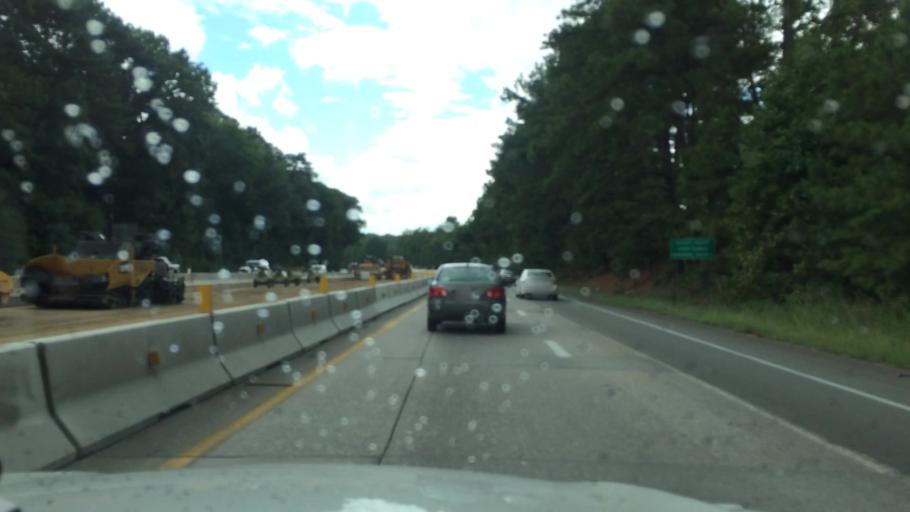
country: US
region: South Carolina
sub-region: Lexington County
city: Oak Grove
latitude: 34.0039
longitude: -81.1673
